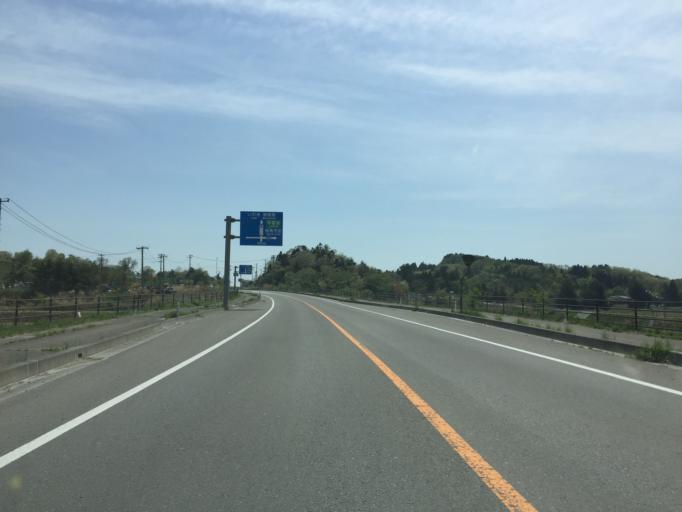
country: JP
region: Miyagi
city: Marumori
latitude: 37.8582
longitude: 140.9198
